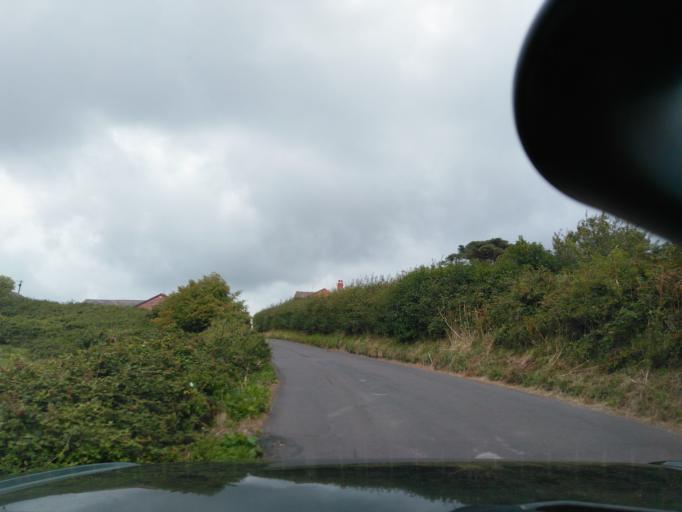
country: GB
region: England
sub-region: Dorset
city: Swanage
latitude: 50.6338
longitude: -1.9820
